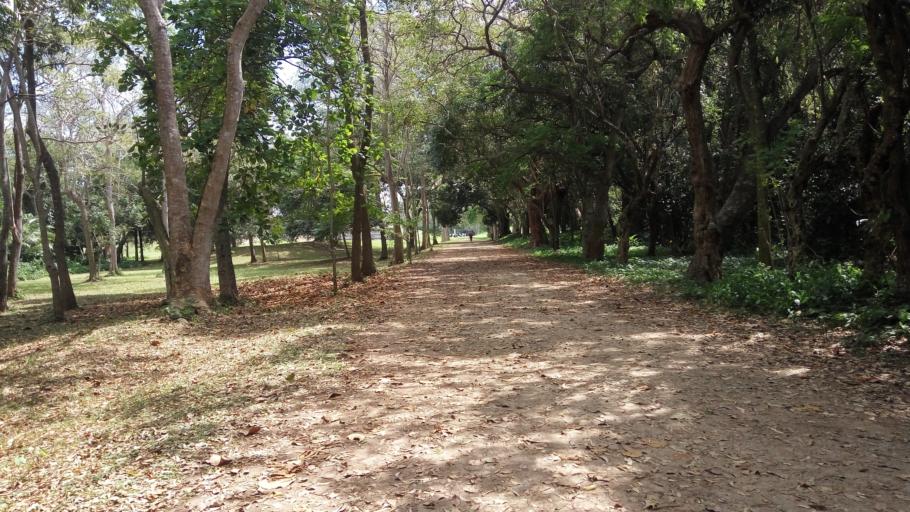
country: MX
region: Tabasco
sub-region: Comalcalco
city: Oriente 1ra. Seccion (Santo Domingo)
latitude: 18.2798
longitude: -93.2035
